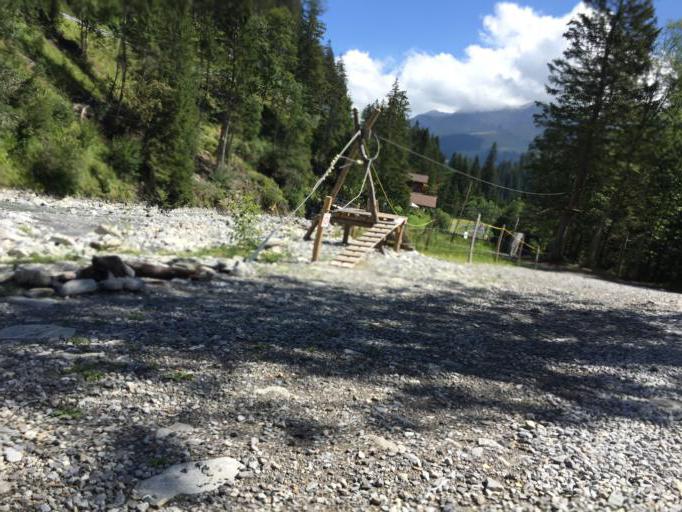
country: CH
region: Bern
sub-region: Frutigen-Niedersimmental District
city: Adelboden
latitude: 46.4836
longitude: 7.5433
